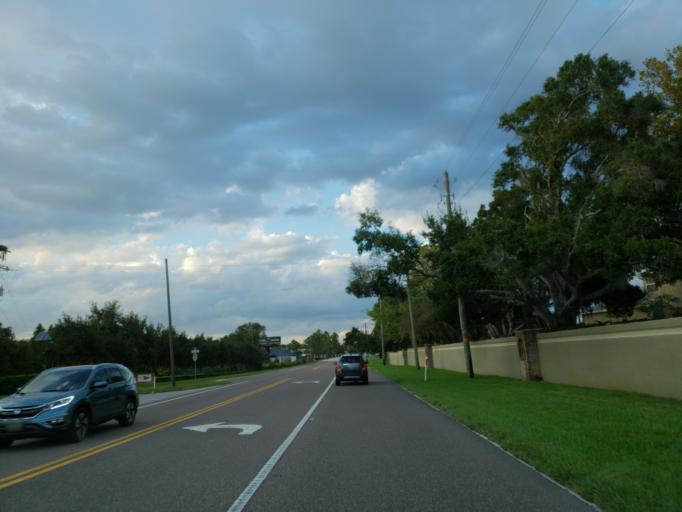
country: US
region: Florida
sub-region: Pasco County
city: Odessa
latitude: 28.1783
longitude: -82.5922
